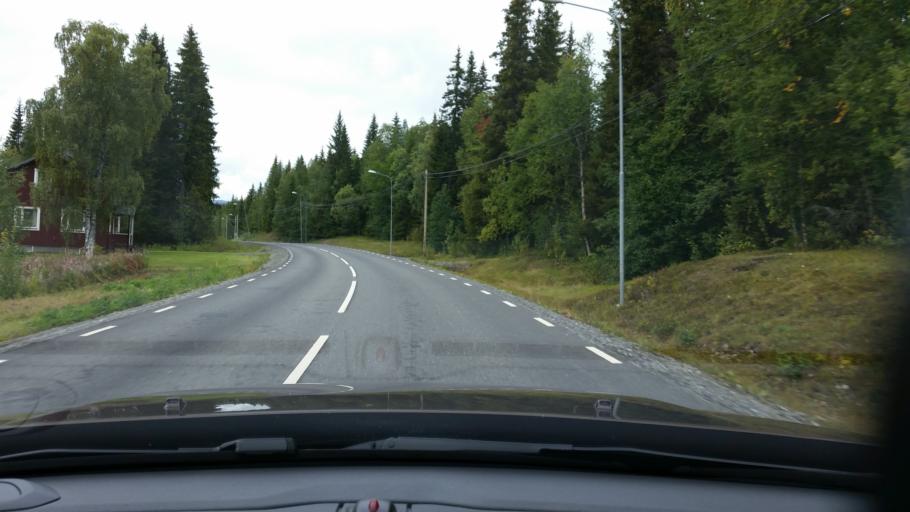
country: NO
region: Nord-Trondelag
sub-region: Lierne
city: Sandvika
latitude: 64.6929
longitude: 14.0806
